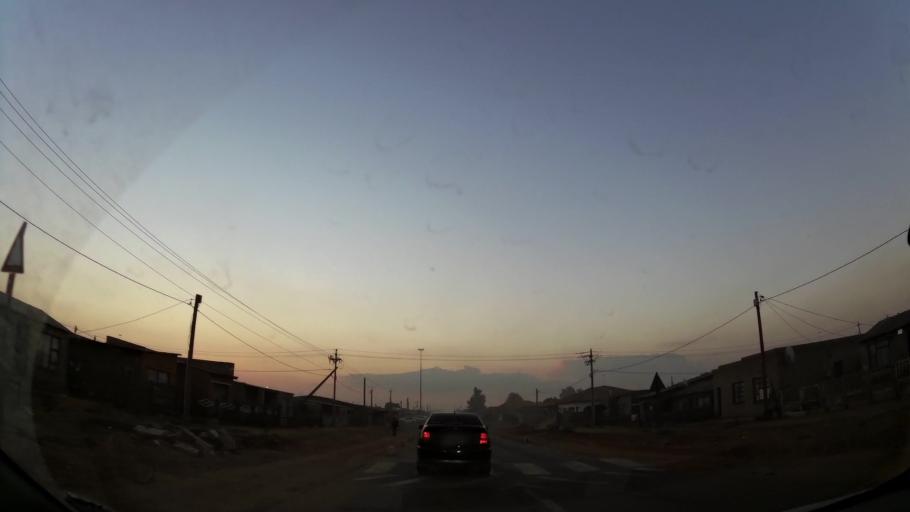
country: ZA
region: Gauteng
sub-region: Ekurhuleni Metropolitan Municipality
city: Springs
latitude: -26.3552
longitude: 28.3836
